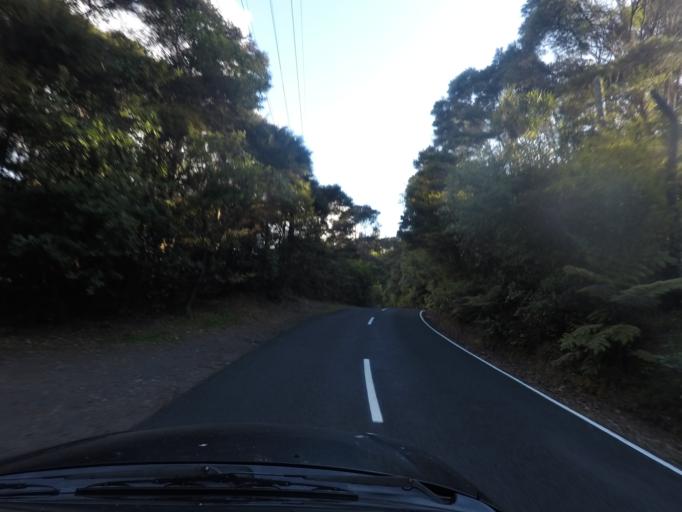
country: NZ
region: Auckland
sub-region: Auckland
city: Titirangi
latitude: -36.9341
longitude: 174.6189
